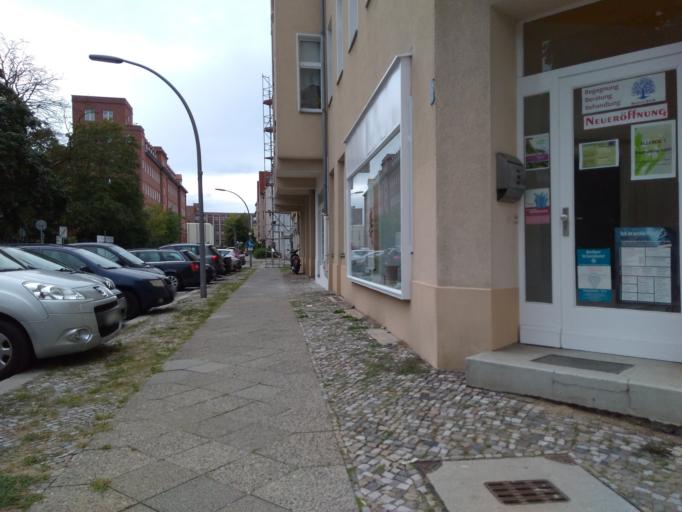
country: DE
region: Berlin
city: Siemensstadt
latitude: 52.5354
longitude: 13.2686
